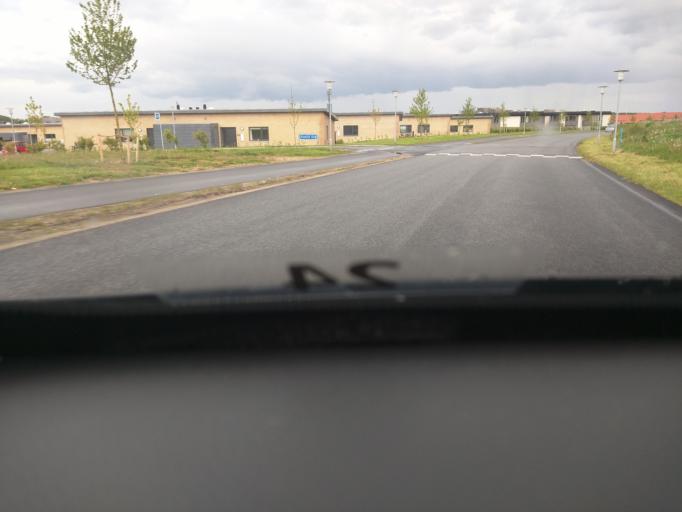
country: DK
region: Central Jutland
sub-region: Viborg Kommune
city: Viborg
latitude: 56.4534
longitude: 9.4576
